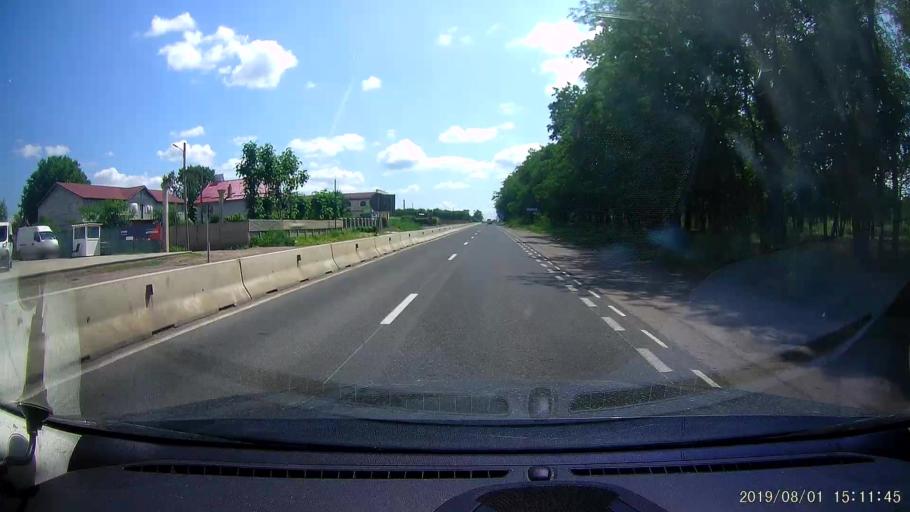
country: RO
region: Braila
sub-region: Comuna Chiscani
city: Chiscani
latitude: 45.2147
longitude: 27.9214
